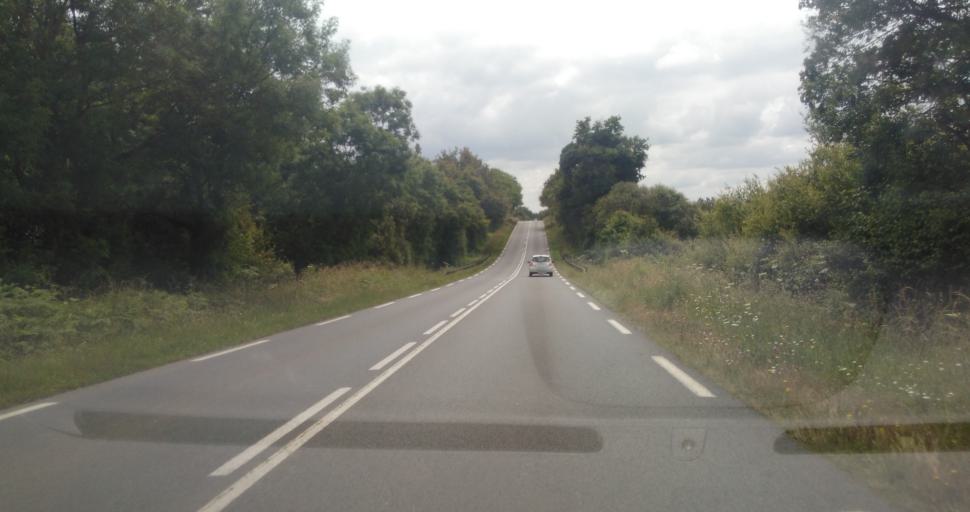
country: FR
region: Pays de la Loire
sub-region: Departement de la Vendee
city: Bournezeau
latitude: 46.6141
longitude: -1.1479
